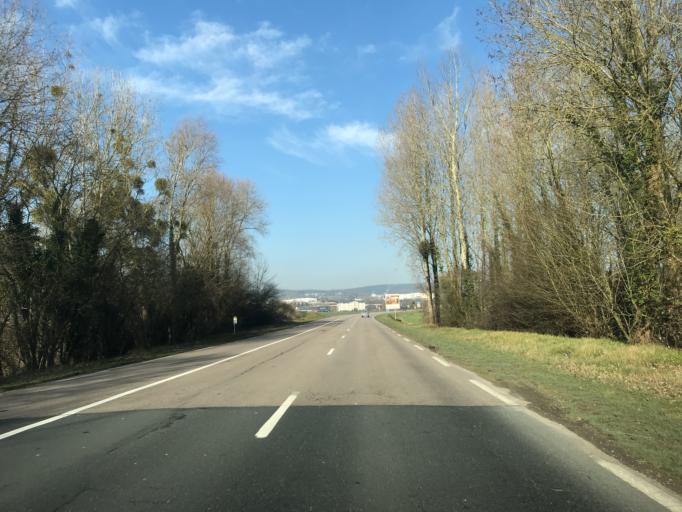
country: FR
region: Haute-Normandie
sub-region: Departement de l'Eure
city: Le Vaudreuil
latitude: 49.2434
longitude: 1.1945
